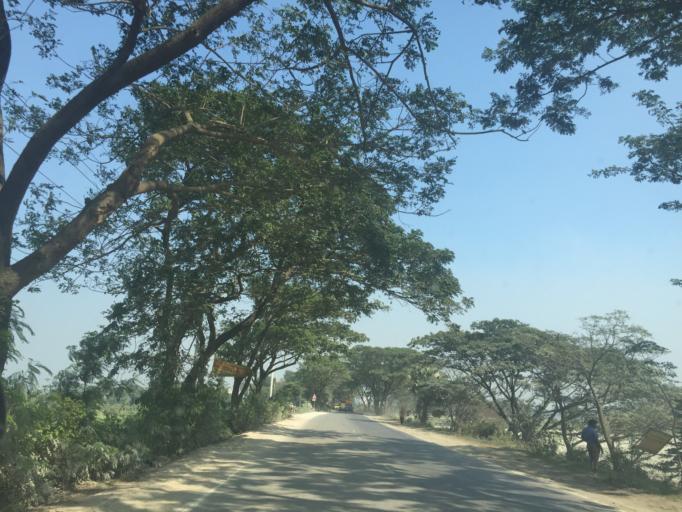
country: BD
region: Dhaka
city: Tungi
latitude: 23.8393
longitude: 90.3414
